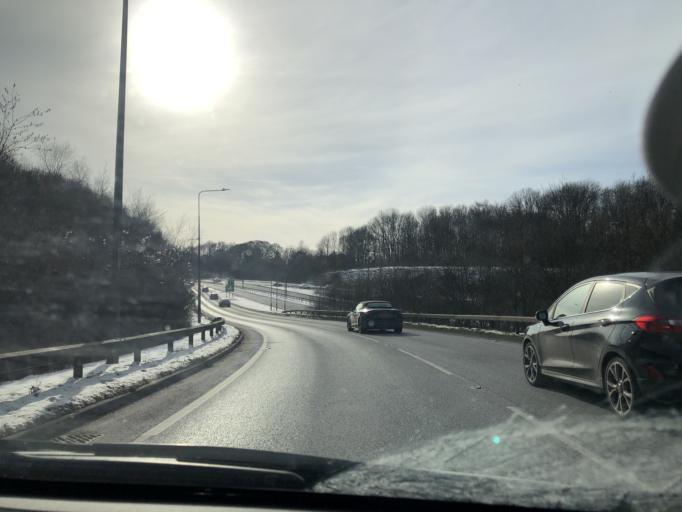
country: GB
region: England
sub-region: Kent
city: Aylesford
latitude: 51.3359
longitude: 0.5046
